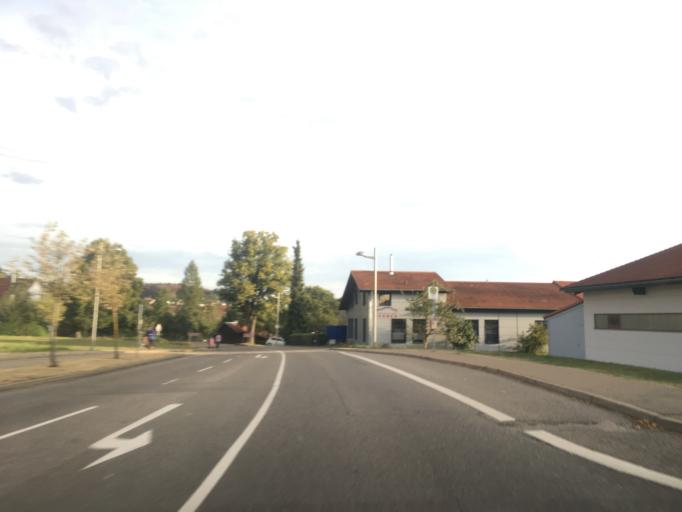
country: DE
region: Baden-Wuerttemberg
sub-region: Tuebingen Region
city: Sankt Johann
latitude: 48.4594
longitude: 9.3403
